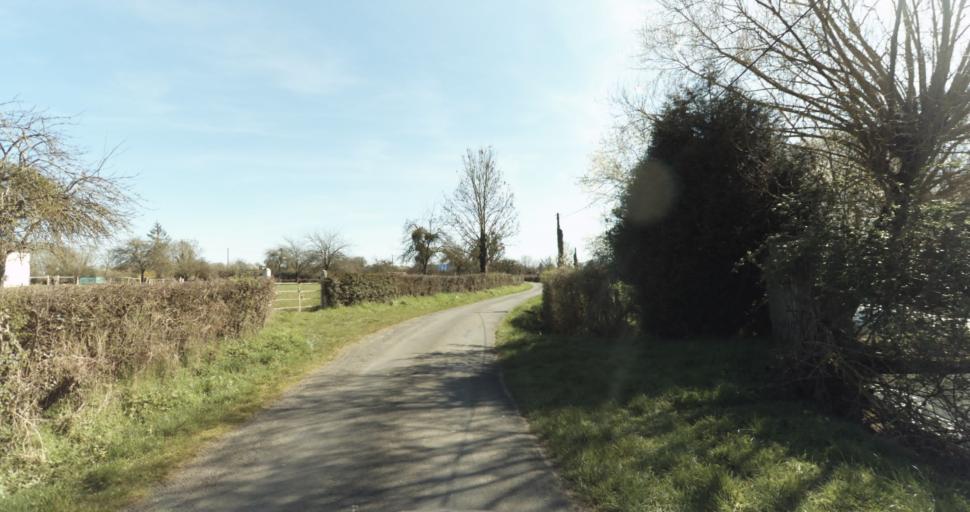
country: FR
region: Lower Normandy
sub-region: Departement du Calvados
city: Saint-Pierre-sur-Dives
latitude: 49.0624
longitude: -0.0278
